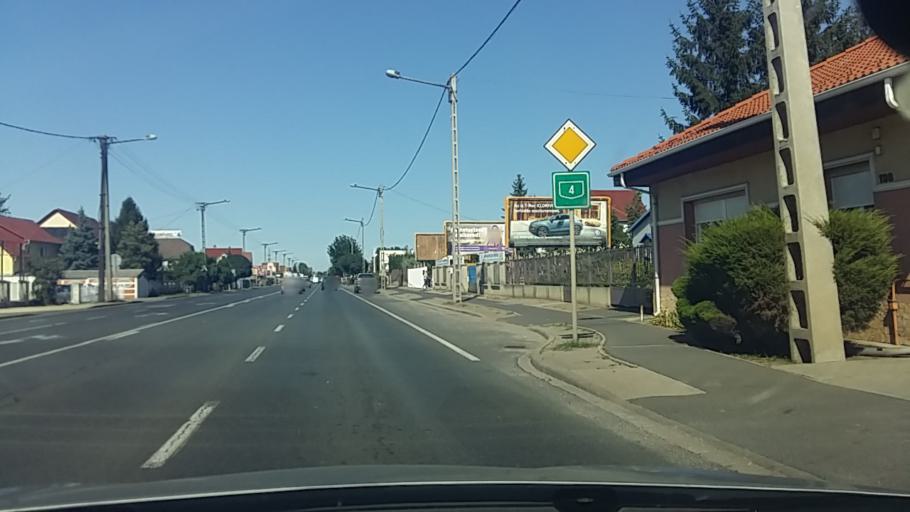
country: HU
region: Szabolcs-Szatmar-Bereg
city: Nyiregyhaza
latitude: 47.9259
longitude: 21.7187
